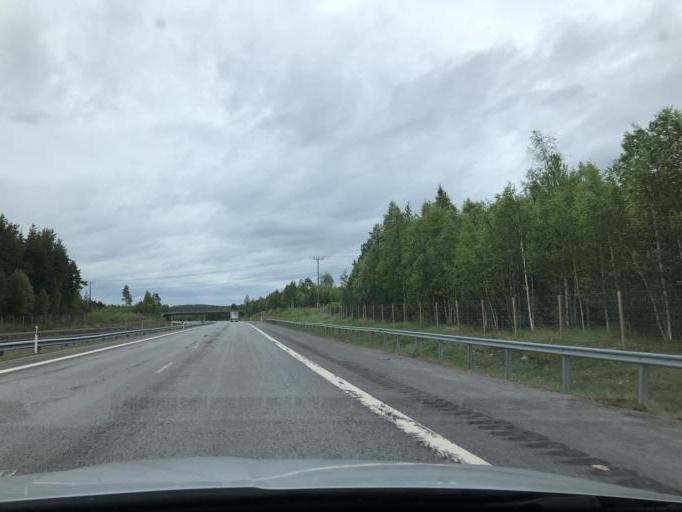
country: SE
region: Norrbotten
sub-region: Pitea Kommun
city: Pitea
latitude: 65.3473
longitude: 21.4380
